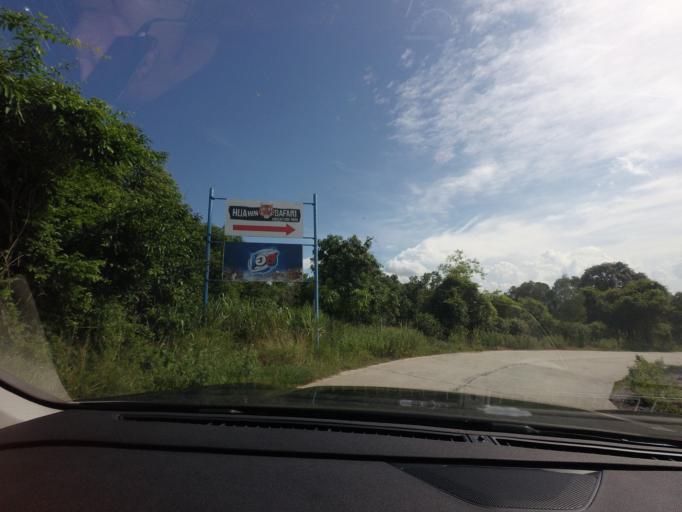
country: TH
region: Prachuap Khiri Khan
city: Hua Hin
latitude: 12.4862
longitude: 99.9423
